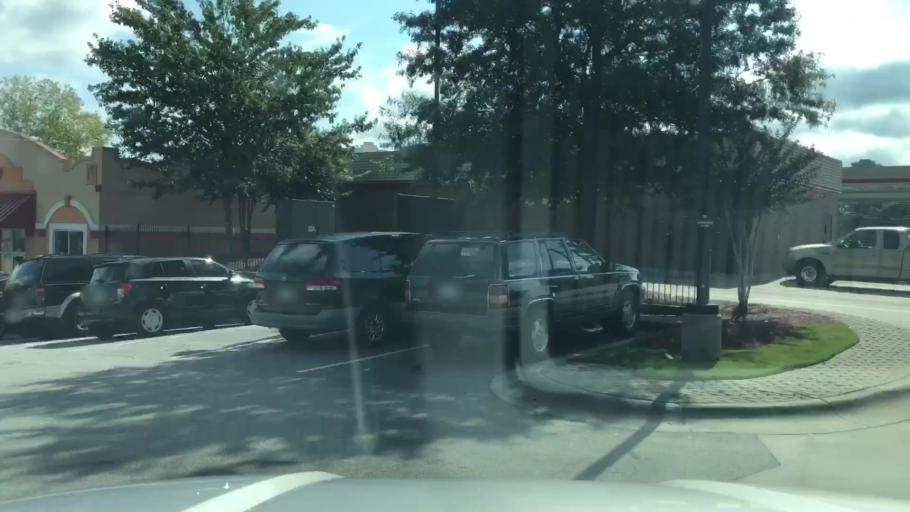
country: US
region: Georgia
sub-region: DeKalb County
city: North Atlanta
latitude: 33.8616
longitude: -84.3095
